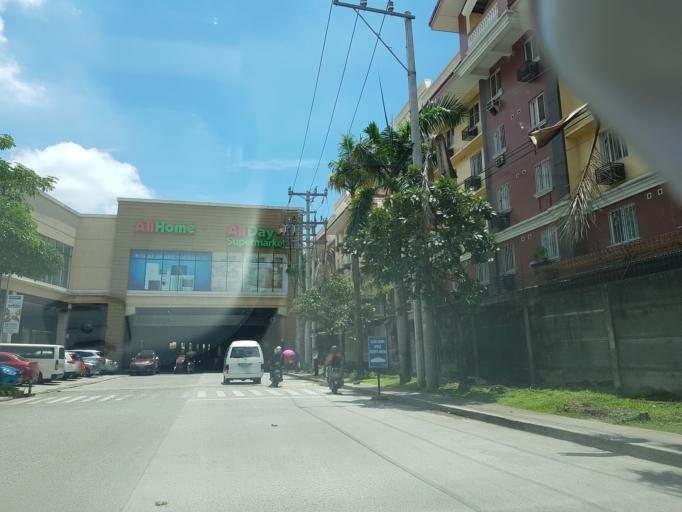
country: PH
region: Calabarzon
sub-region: Province of Rizal
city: Pateros
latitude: 14.5315
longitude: 121.0724
